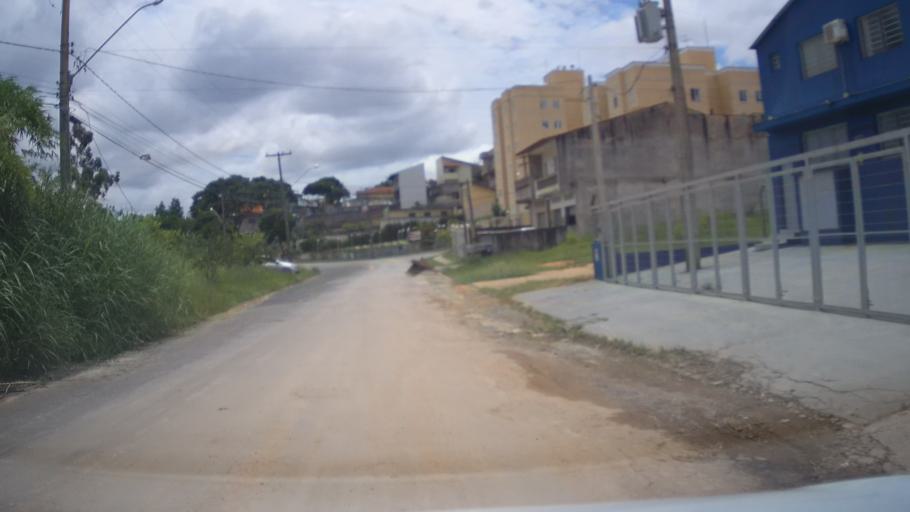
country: BR
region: Sao Paulo
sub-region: Valinhos
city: Valinhos
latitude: -22.9895
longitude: -46.9881
